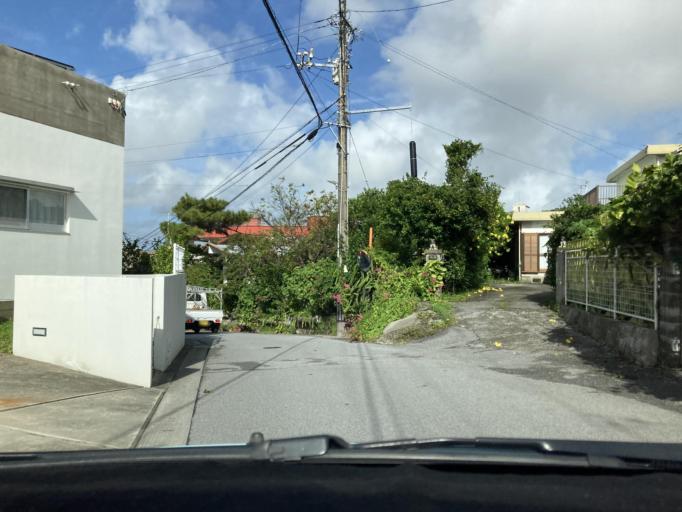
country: JP
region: Okinawa
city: Naha-shi
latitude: 26.2054
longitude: 127.7298
